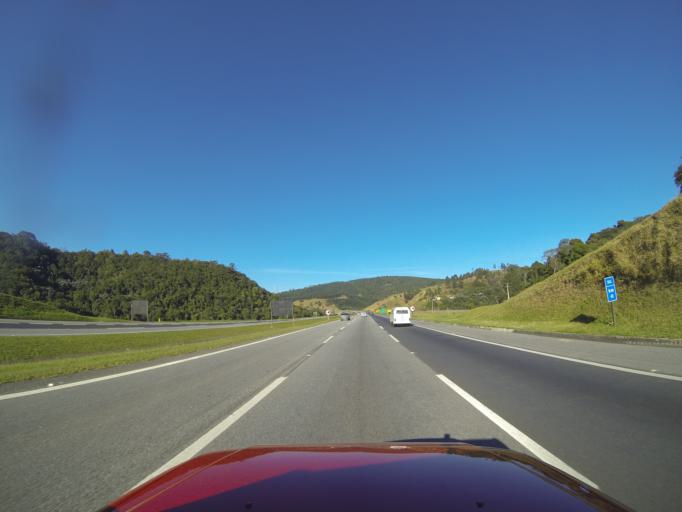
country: BR
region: Sao Paulo
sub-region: Piracaia
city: Piracaia
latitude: -23.1816
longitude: -46.3018
